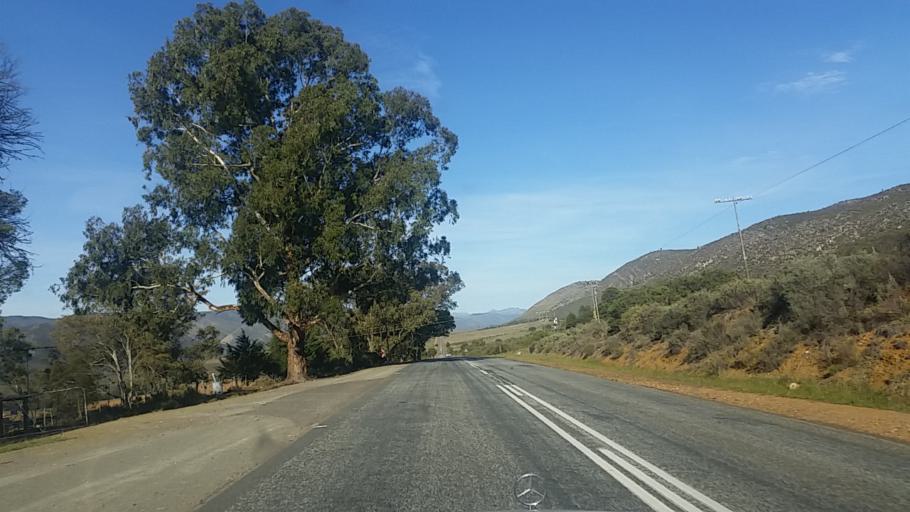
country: ZA
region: Western Cape
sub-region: Eden District Municipality
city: Knysna
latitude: -33.7729
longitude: 22.9196
